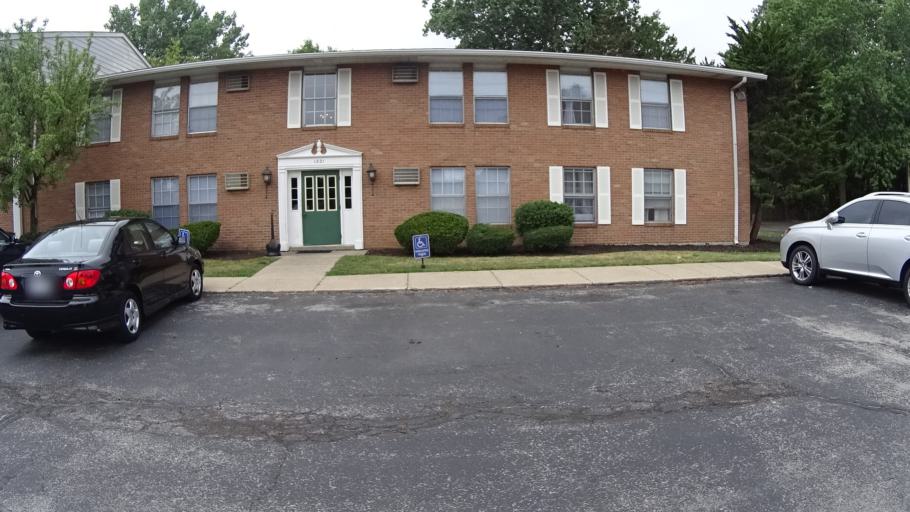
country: US
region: Ohio
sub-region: Erie County
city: Sandusky
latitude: 41.4418
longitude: -82.6926
